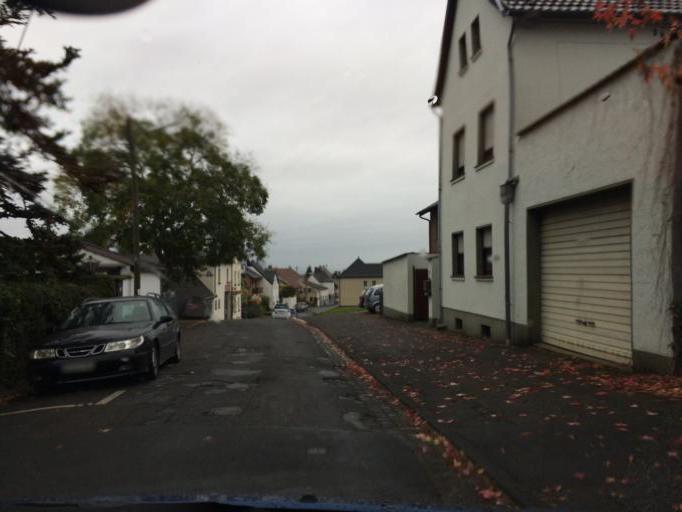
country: DE
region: North Rhine-Westphalia
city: Bruhl
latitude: 50.7736
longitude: 6.9236
